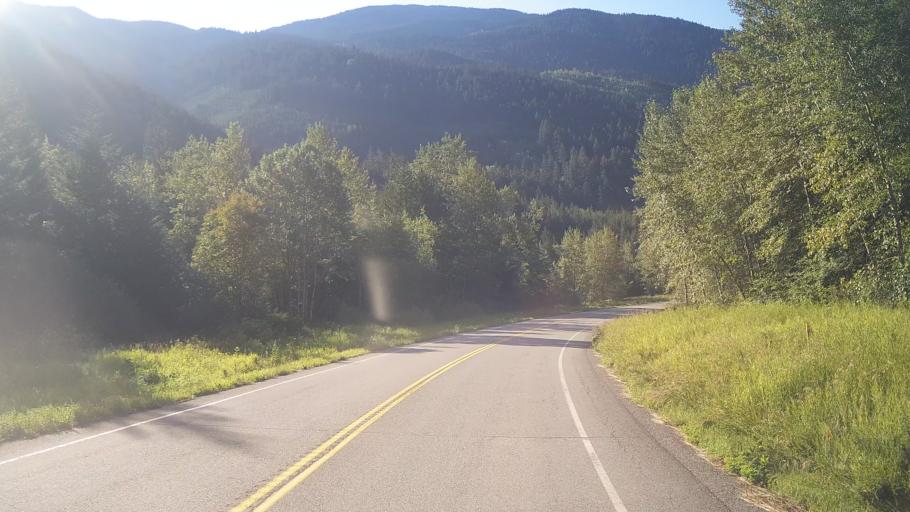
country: CA
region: British Columbia
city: Lillooet
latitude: 50.5818
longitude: -122.0891
